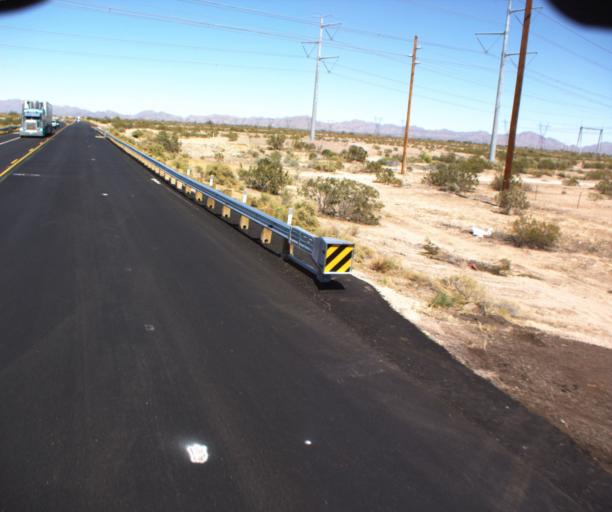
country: US
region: Arizona
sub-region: Maricopa County
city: Gila Bend
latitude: 32.9707
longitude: -112.6729
